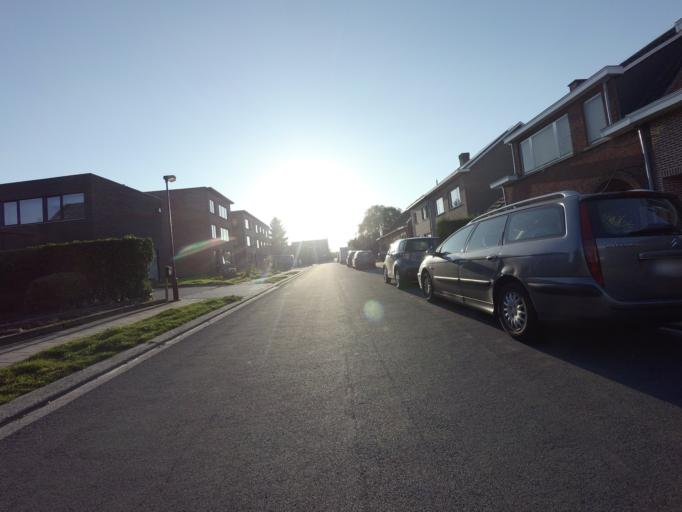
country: BE
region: Flanders
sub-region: Provincie Antwerpen
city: Lint
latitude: 51.1338
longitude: 4.4824
